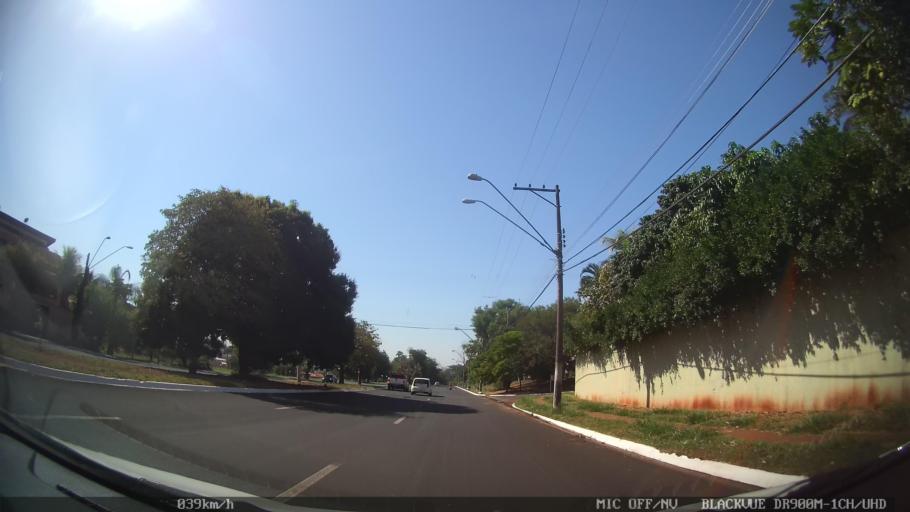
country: BR
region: Sao Paulo
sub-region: Ribeirao Preto
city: Ribeirao Preto
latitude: -21.2164
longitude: -47.7874
